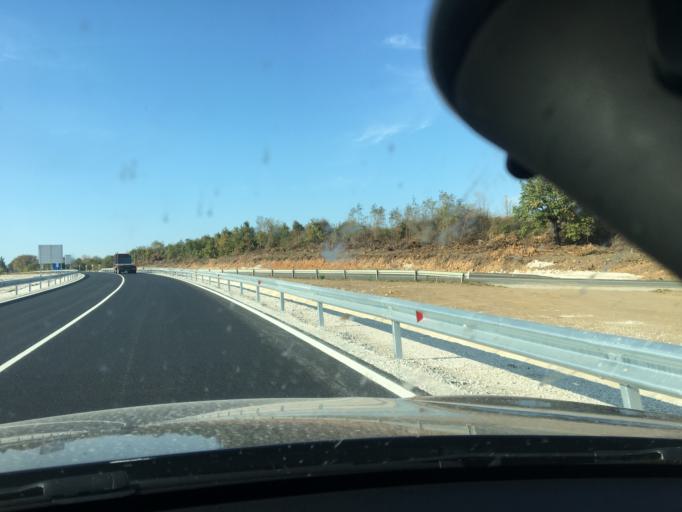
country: BG
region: Lovech
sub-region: Obshtina Yablanitsa
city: Yablanitsa
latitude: 43.0571
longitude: 24.2218
